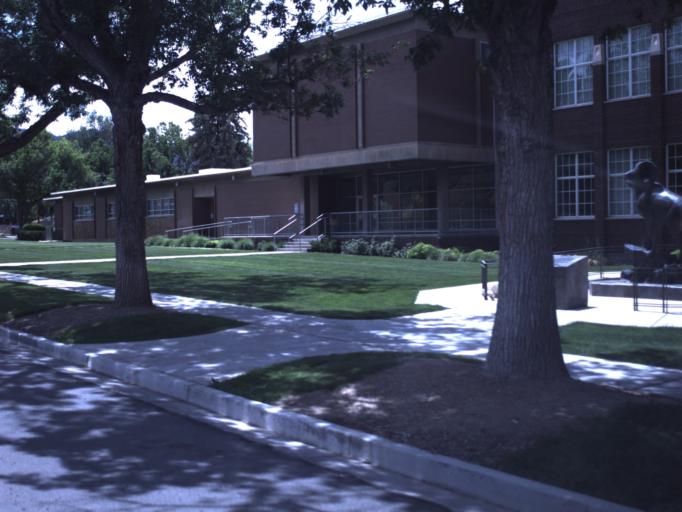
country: US
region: Utah
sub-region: Iron County
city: Parowan
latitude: 37.8454
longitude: -112.8277
